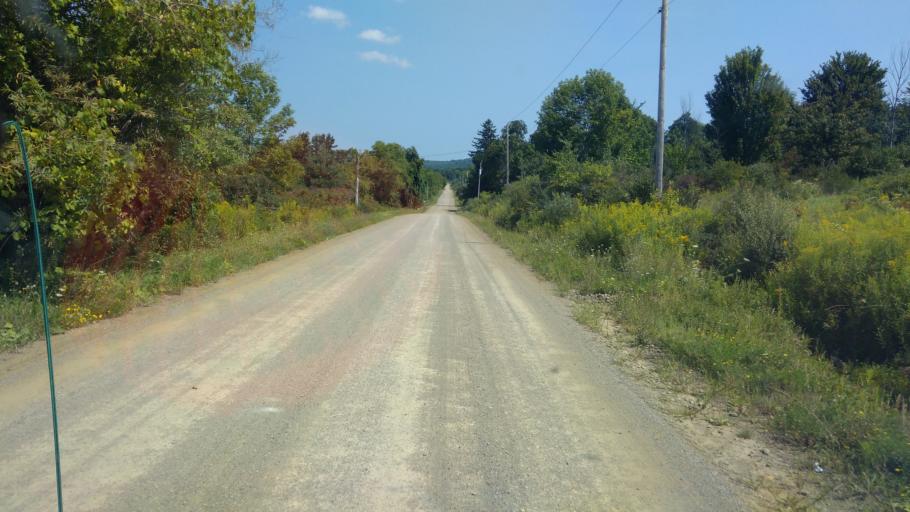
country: US
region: New York
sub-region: Allegany County
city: Houghton
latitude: 42.3525
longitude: -78.0599
